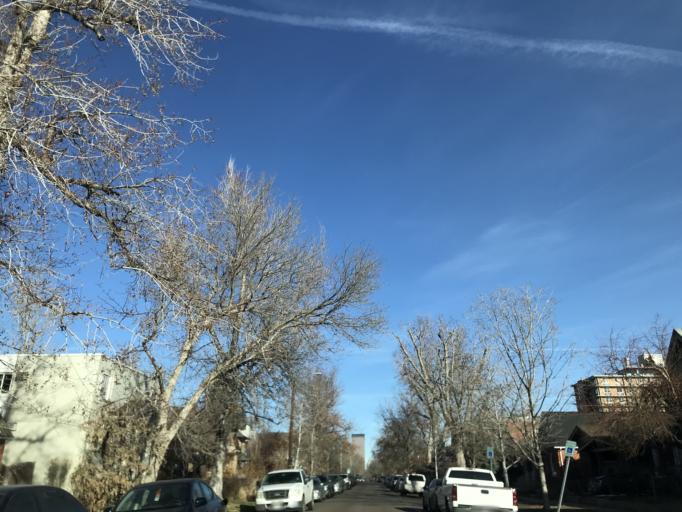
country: US
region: Colorado
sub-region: Denver County
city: Denver
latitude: 39.7170
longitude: -104.9850
